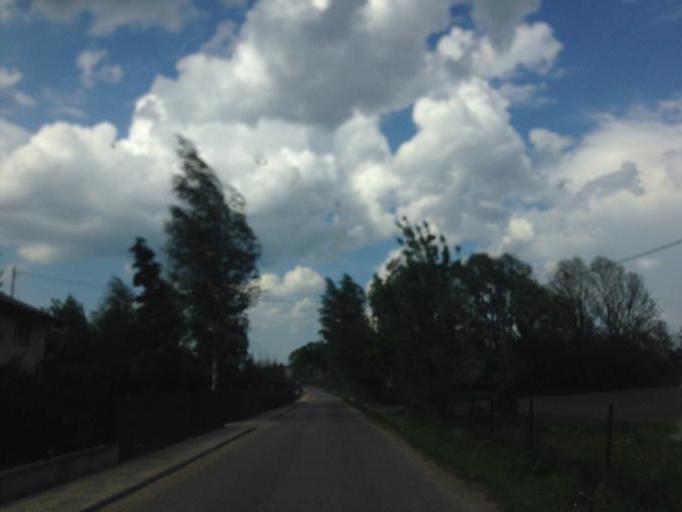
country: PL
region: Warmian-Masurian Voivodeship
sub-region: Powiat nowomiejski
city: Kurzetnik
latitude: 53.4406
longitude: 19.5144
